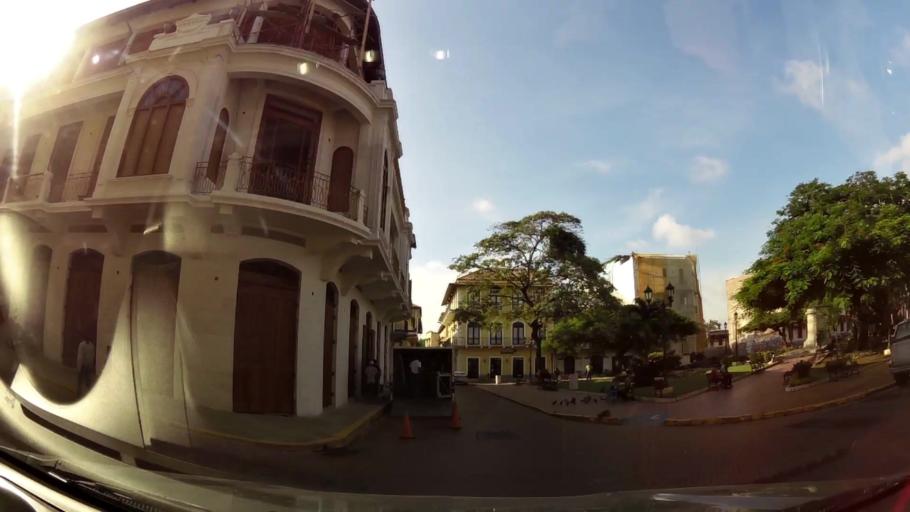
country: PA
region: Panama
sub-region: Distrito de Panama
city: Ancon
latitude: 8.9522
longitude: -79.5365
